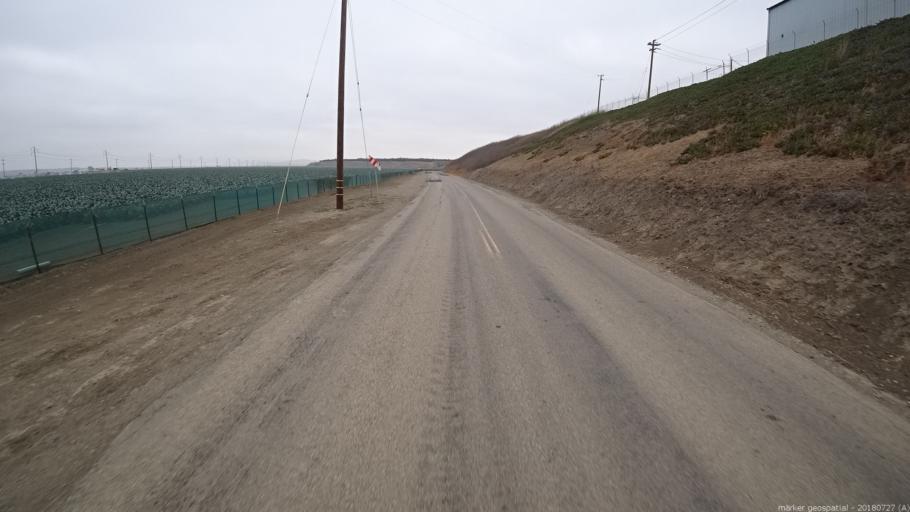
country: US
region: California
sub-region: Monterey County
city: King City
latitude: 36.2311
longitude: -121.1290
